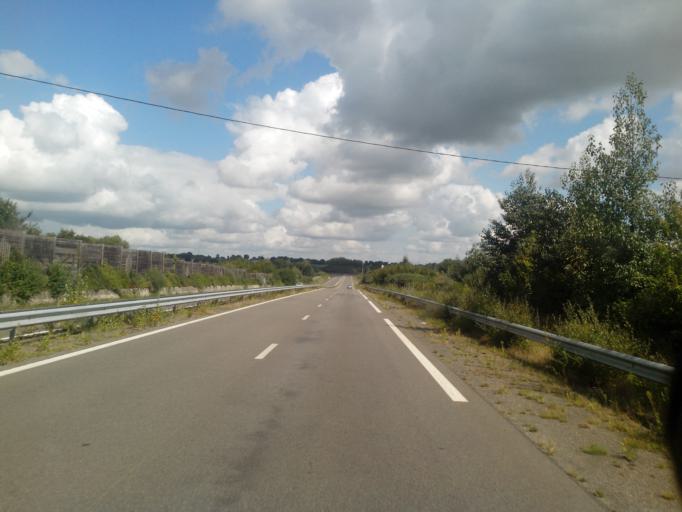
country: FR
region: Brittany
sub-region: Departement d'Ille-et-Vilaine
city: Chevaigne
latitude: 48.1932
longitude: -1.6223
